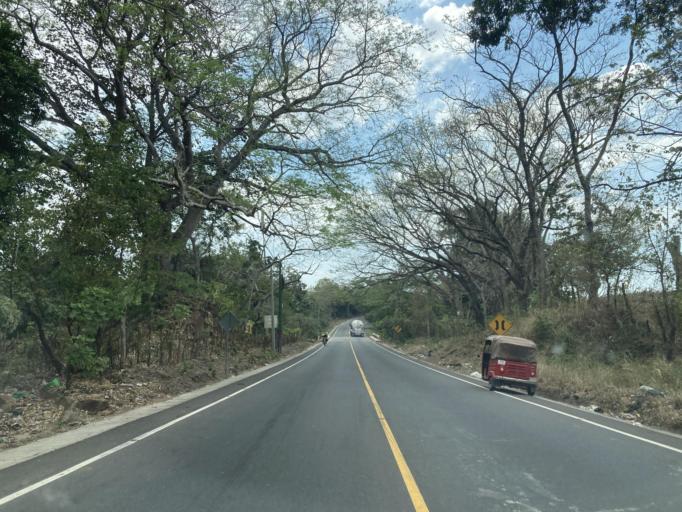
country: GT
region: Santa Rosa
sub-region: Municipio de Taxisco
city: Taxisco
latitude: 14.0842
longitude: -90.4923
